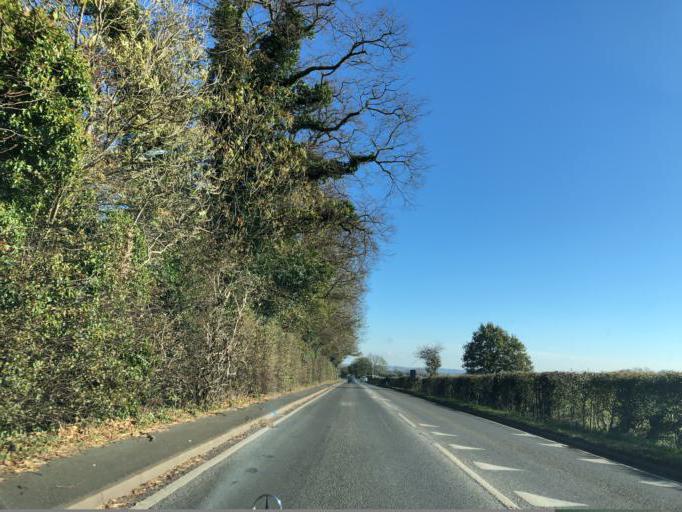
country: GB
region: England
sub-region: Warwickshire
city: Harbury
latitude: 52.2556
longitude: -1.4434
